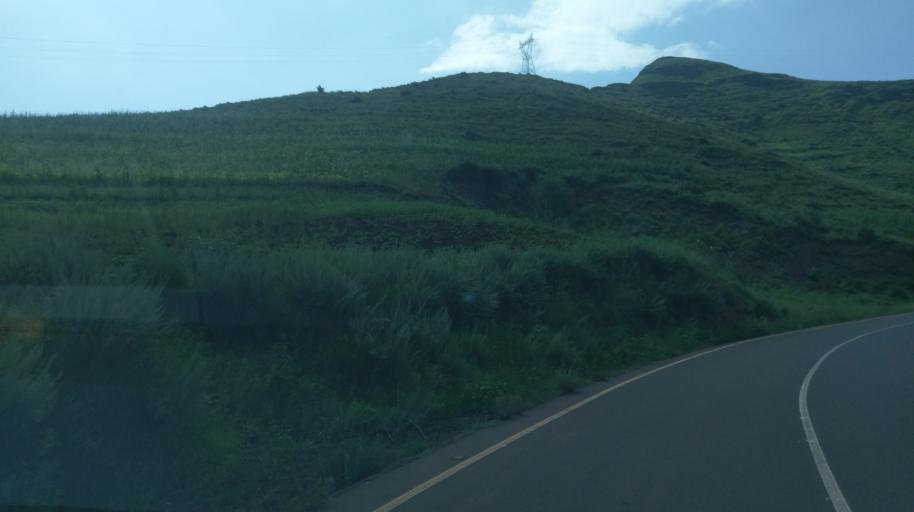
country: LS
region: Thaba-Tseka
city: Thaba-Tseka
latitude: -29.1549
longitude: 28.4800
